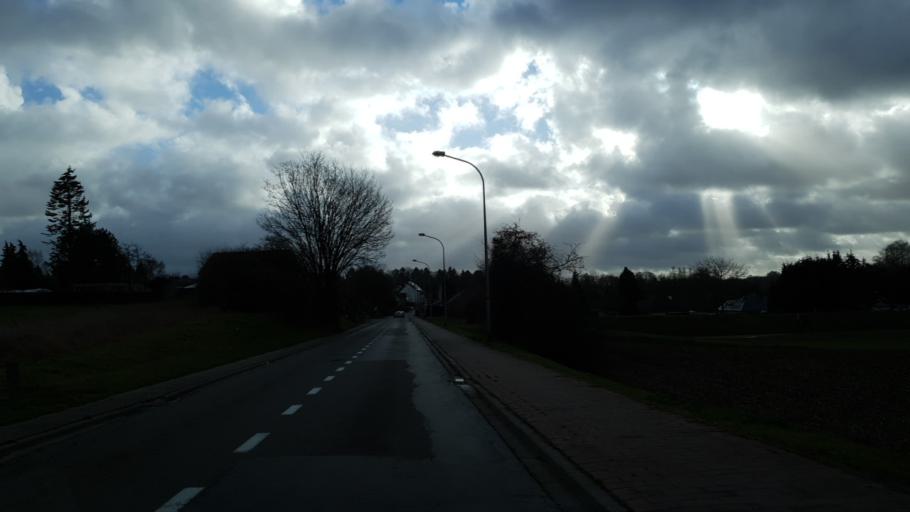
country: BE
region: Flanders
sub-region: Provincie Vlaams-Brabant
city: Tervuren
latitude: 50.8410
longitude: 4.5375
